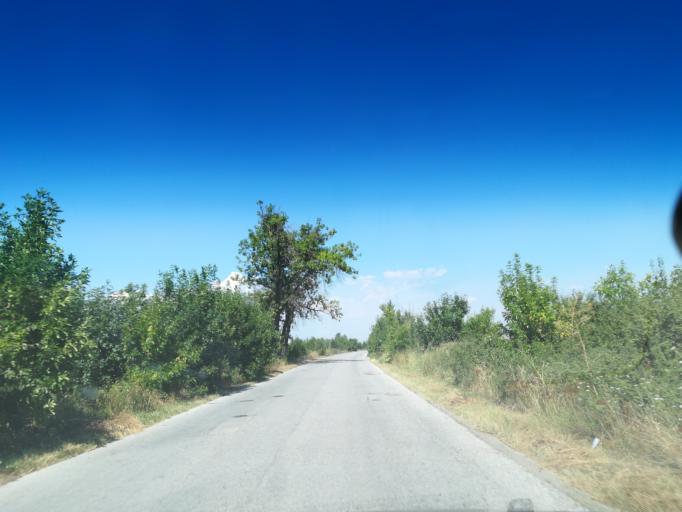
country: BG
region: Stara Zagora
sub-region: Obshtina Chirpan
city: Chirpan
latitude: 42.0578
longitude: 25.1563
